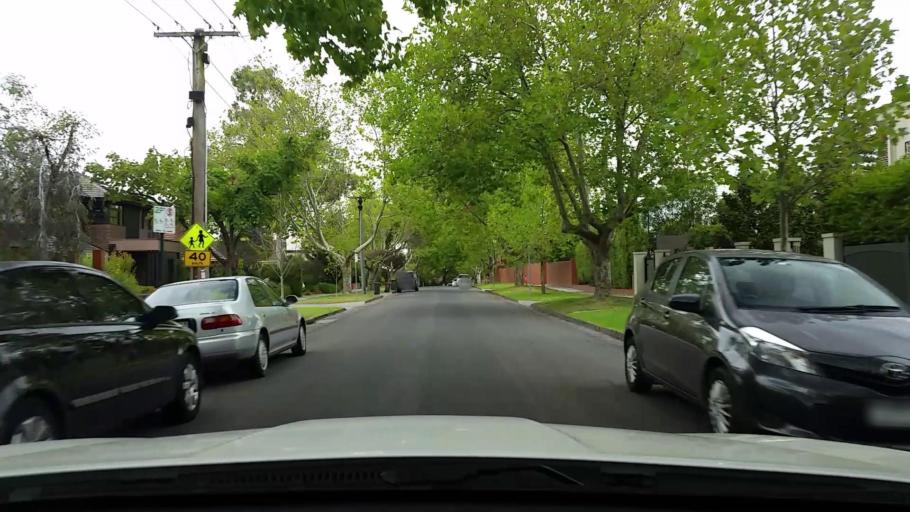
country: AU
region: Victoria
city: Mont Albert
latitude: -37.8191
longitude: 145.1009
